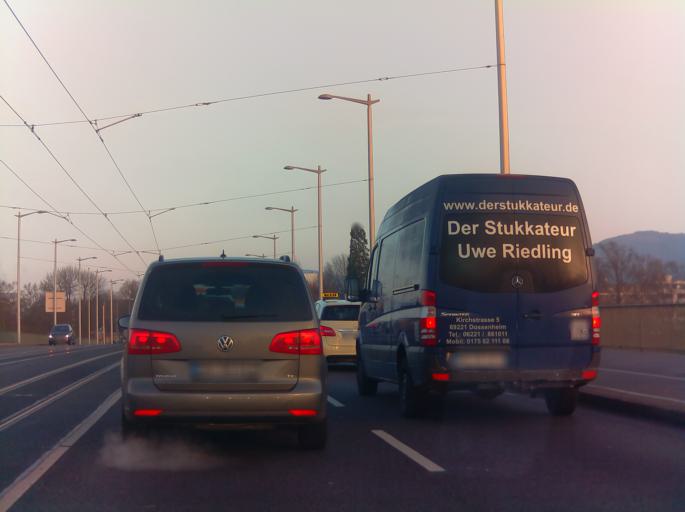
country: DE
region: Baden-Wuerttemberg
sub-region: Karlsruhe Region
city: Heidelberg
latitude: 49.4100
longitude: 8.6769
